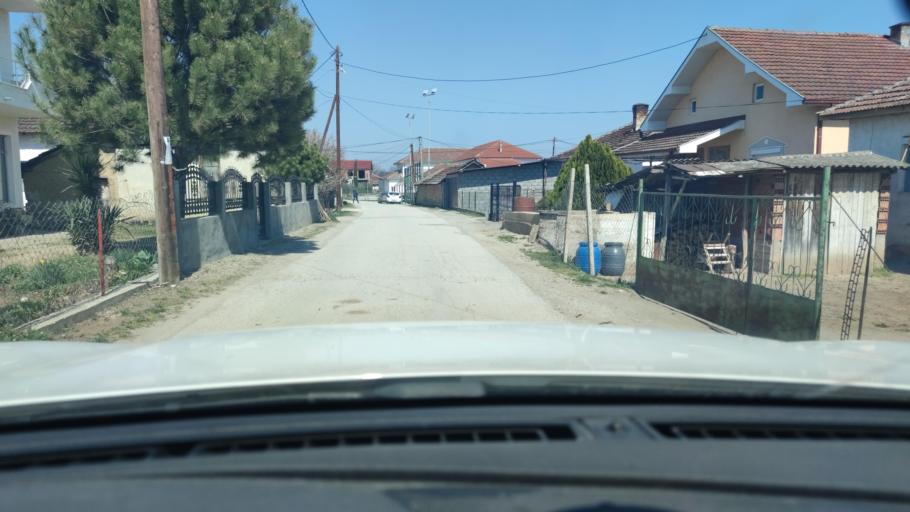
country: MK
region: Rosoman
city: Rosoman
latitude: 41.5174
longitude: 21.9400
